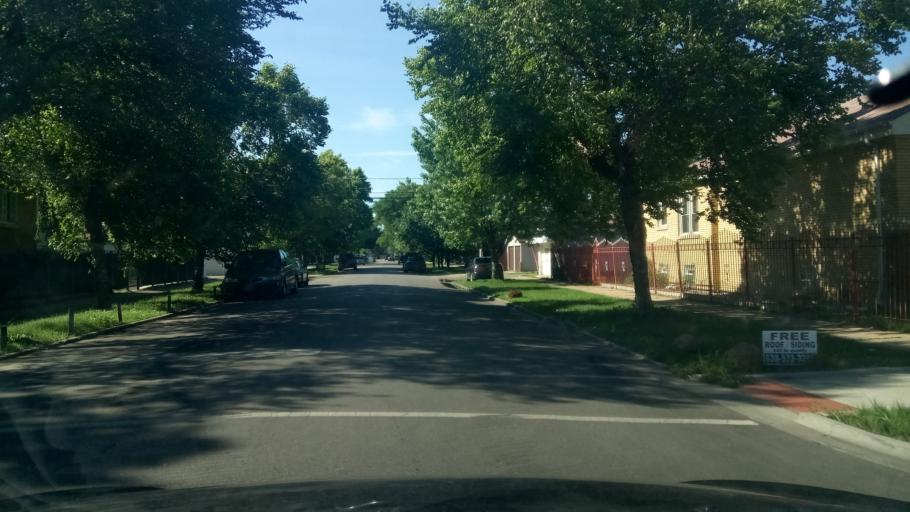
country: US
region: Illinois
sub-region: Cook County
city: Hometown
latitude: 41.7848
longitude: -87.7156
